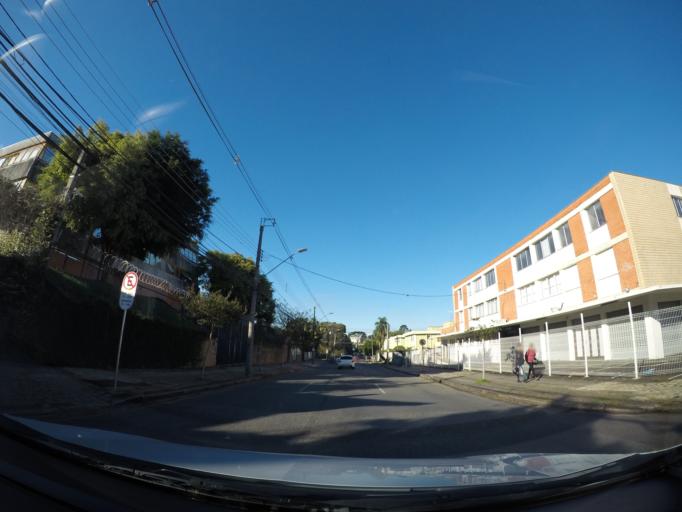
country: BR
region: Parana
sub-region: Curitiba
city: Curitiba
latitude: -25.4142
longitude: -49.2737
